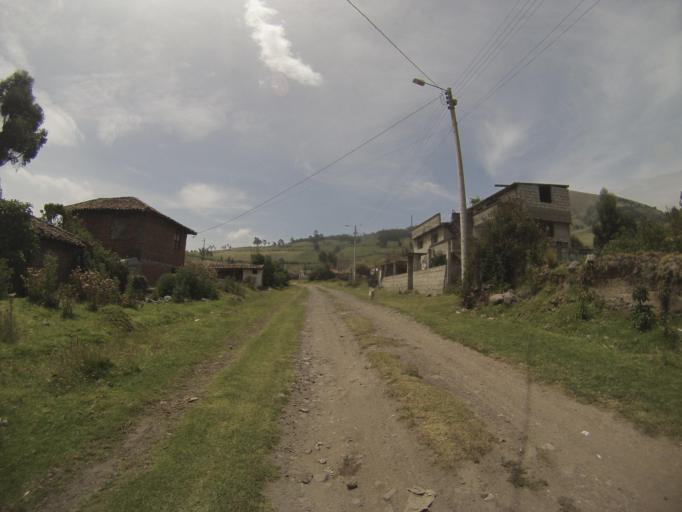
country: EC
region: Pichincha
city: Cayambe
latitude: 0.1546
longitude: -78.0656
